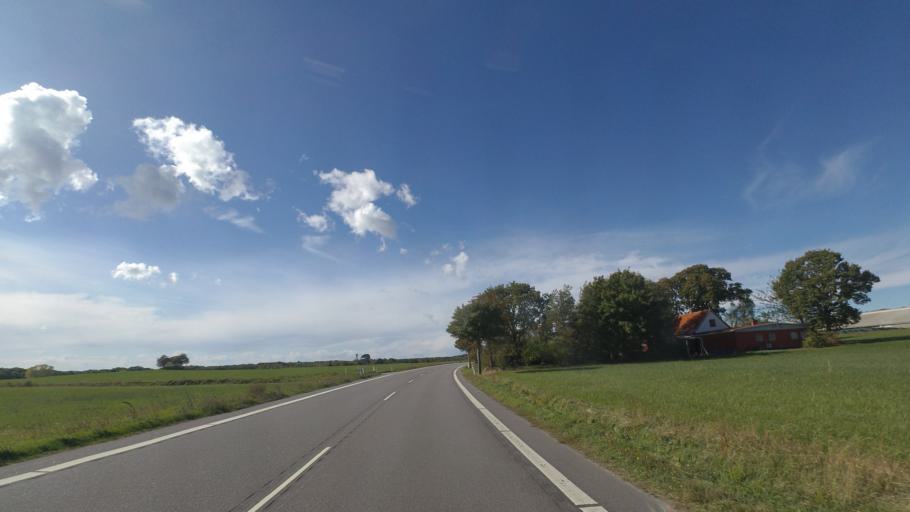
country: DK
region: Capital Region
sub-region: Bornholm Kommune
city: Ronne
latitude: 55.0747
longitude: 14.7824
